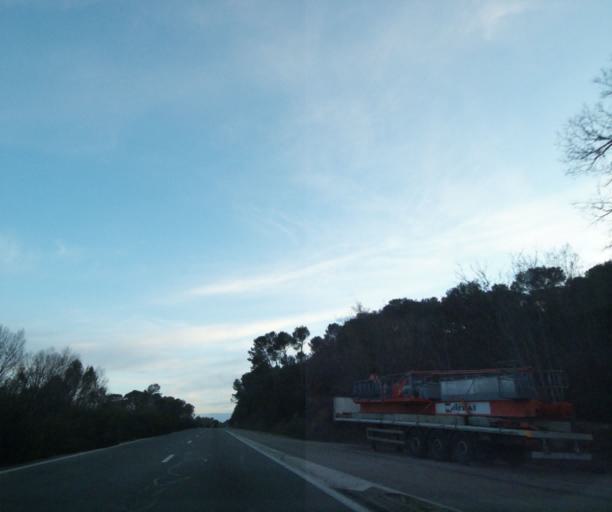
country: FR
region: Provence-Alpes-Cote d'Azur
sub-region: Departement du Var
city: Trans-en-Provence
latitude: 43.4890
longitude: 6.5074
